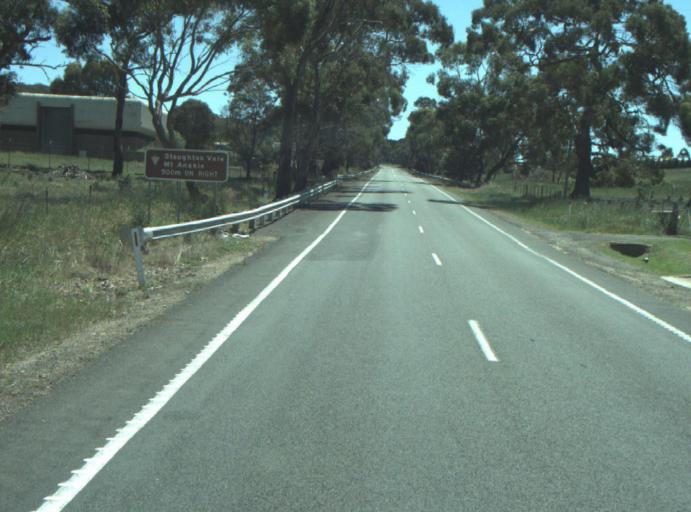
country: AU
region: Victoria
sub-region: Greater Geelong
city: Lara
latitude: -37.8899
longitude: 144.2563
